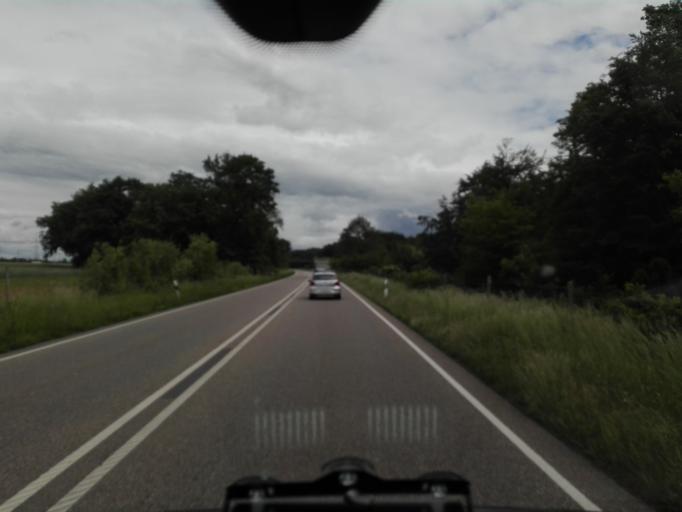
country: DE
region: Baden-Wuerttemberg
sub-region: Karlsruhe Region
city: Linkenheim-Hochstetten
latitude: 49.1079
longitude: 8.4244
